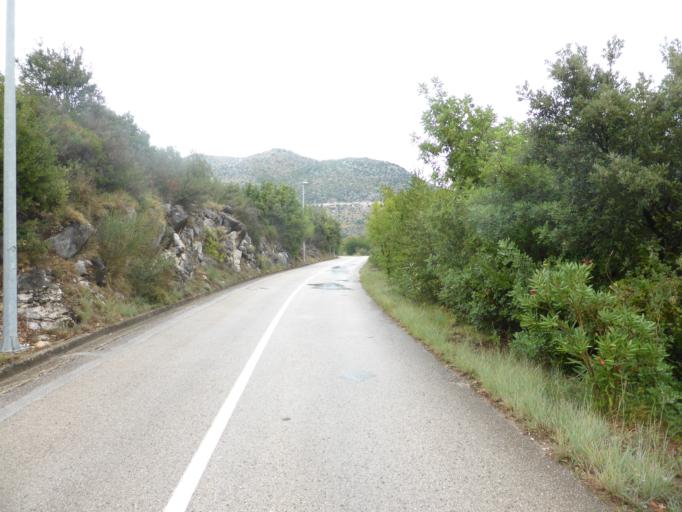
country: HR
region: Dubrovacko-Neretvanska
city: Podgora
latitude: 42.7868
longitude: 17.8794
